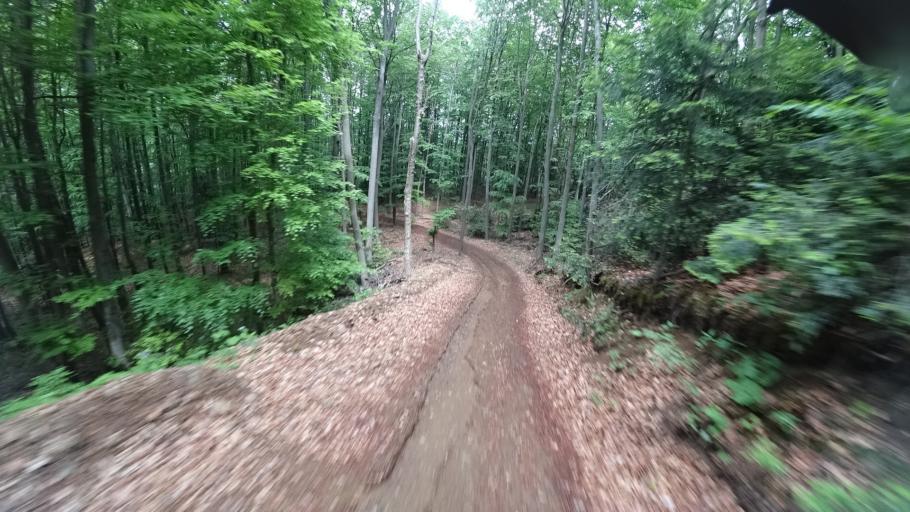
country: HR
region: Grad Zagreb
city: Kasina
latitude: 45.9248
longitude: 15.9425
